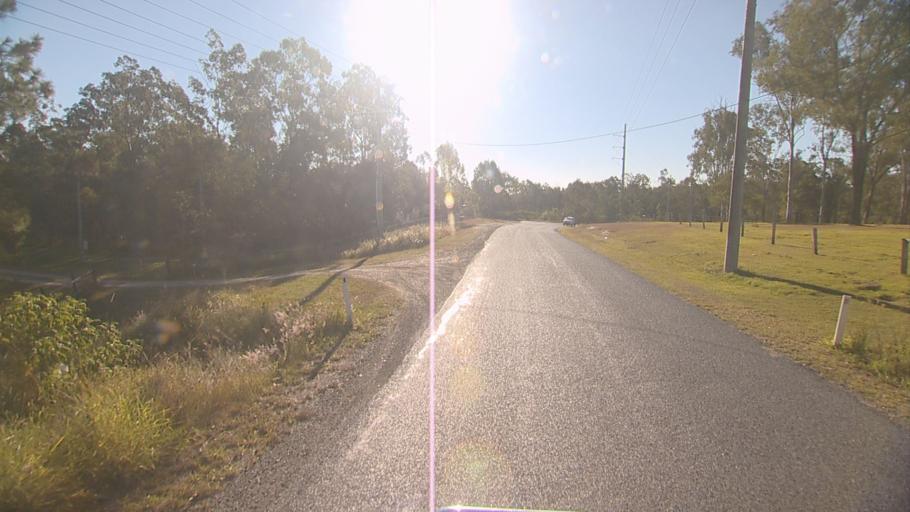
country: AU
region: Queensland
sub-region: Logan
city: North Maclean
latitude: -27.8051
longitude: 153.0413
